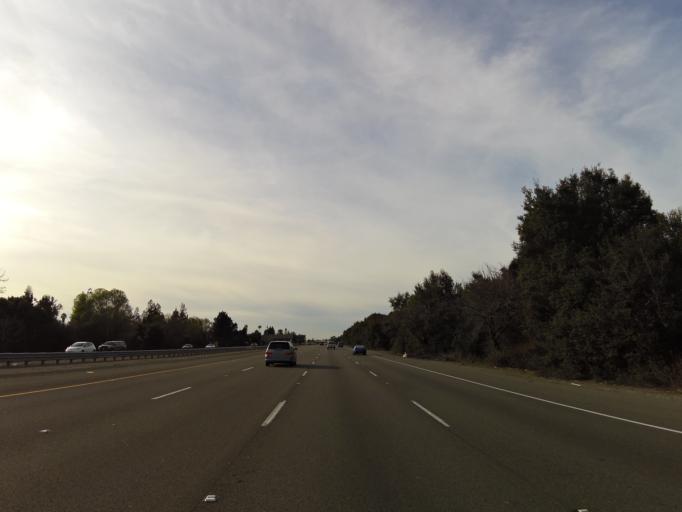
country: US
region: California
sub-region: Santa Clara County
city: Seven Trees
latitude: 37.2502
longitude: -121.7833
